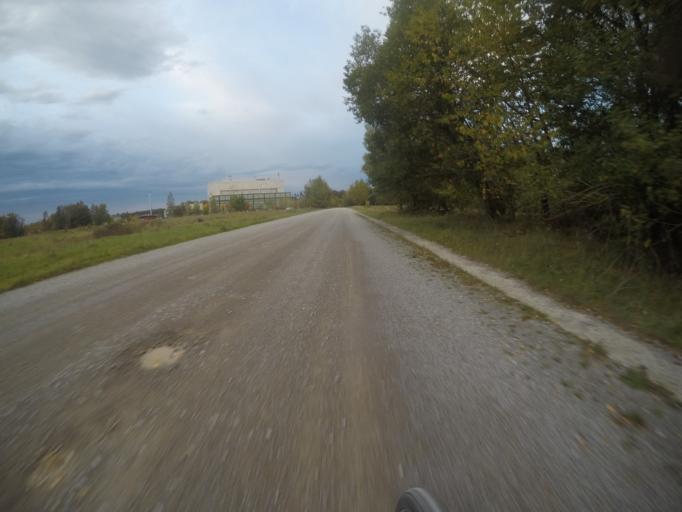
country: DE
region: Baden-Wuerttemberg
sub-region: Regierungsbezirk Stuttgart
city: Schonaich
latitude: 48.6899
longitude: 9.0636
